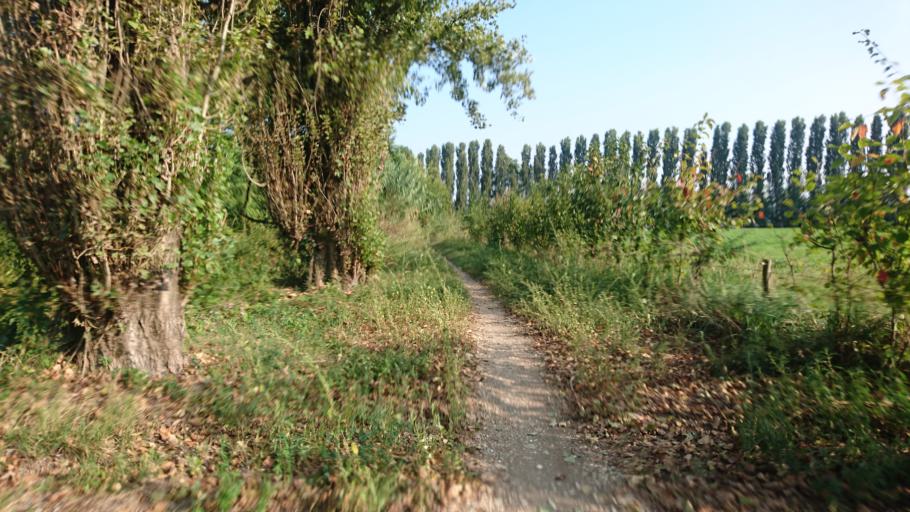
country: IT
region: Veneto
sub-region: Provincia di Padova
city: Tremignon
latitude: 45.5329
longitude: 11.8086
